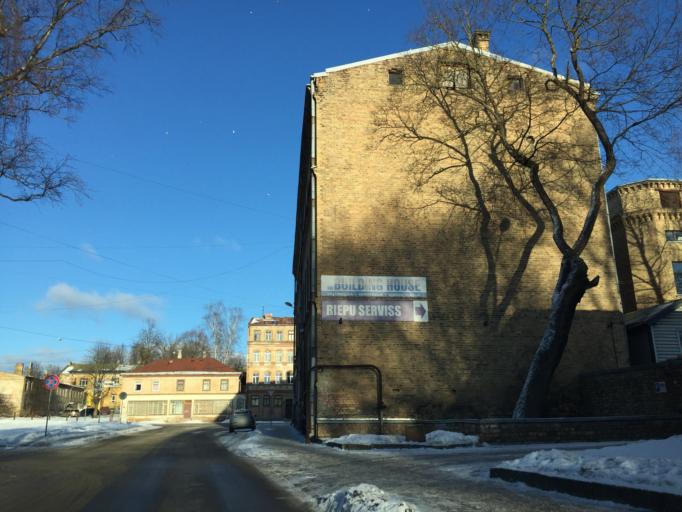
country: LV
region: Riga
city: Riga
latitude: 56.9384
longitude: 24.1395
